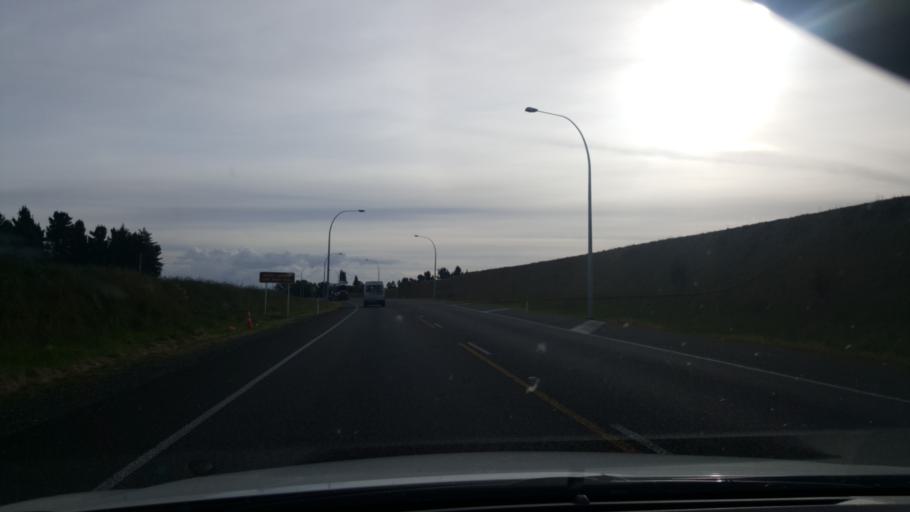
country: NZ
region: Waikato
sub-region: Taupo District
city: Taupo
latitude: -38.7348
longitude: 176.0770
